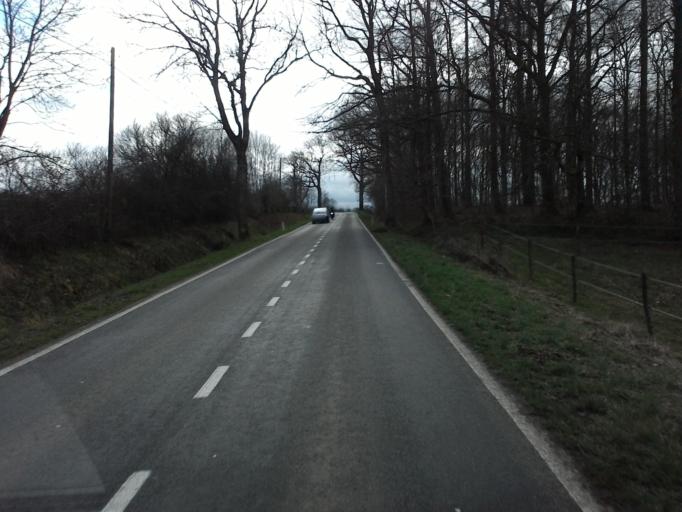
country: BE
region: Wallonia
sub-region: Province de Liege
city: Ferrieres
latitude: 50.3997
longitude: 5.6392
